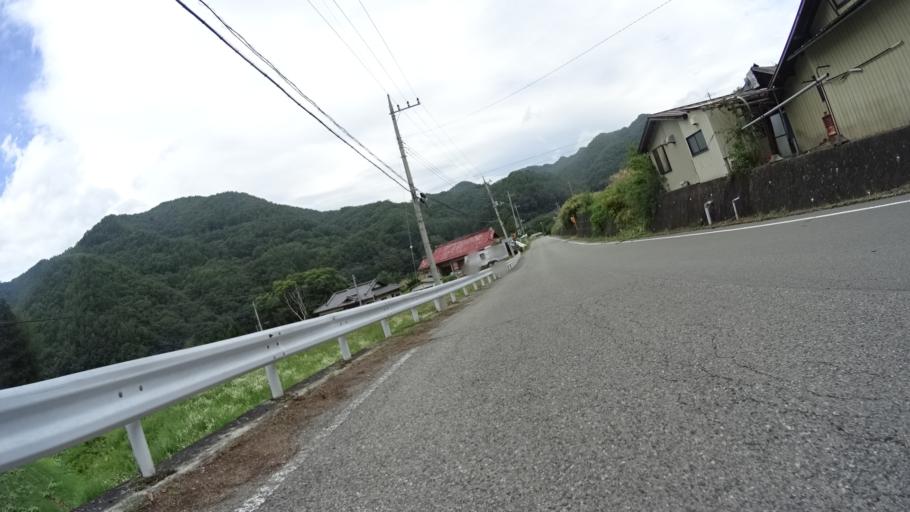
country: JP
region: Yamanashi
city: Nirasaki
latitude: 35.8611
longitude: 138.5230
